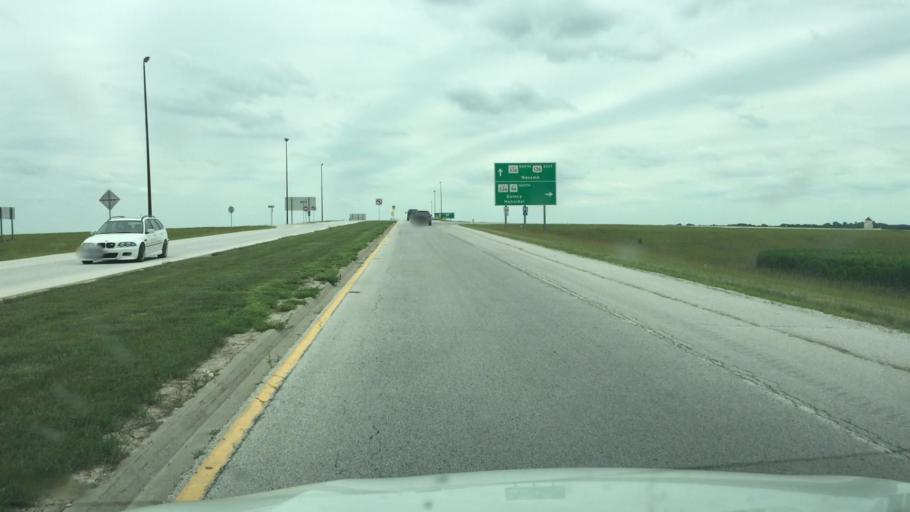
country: US
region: Illinois
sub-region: Hancock County
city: Carthage
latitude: 40.4147
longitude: -91.1147
